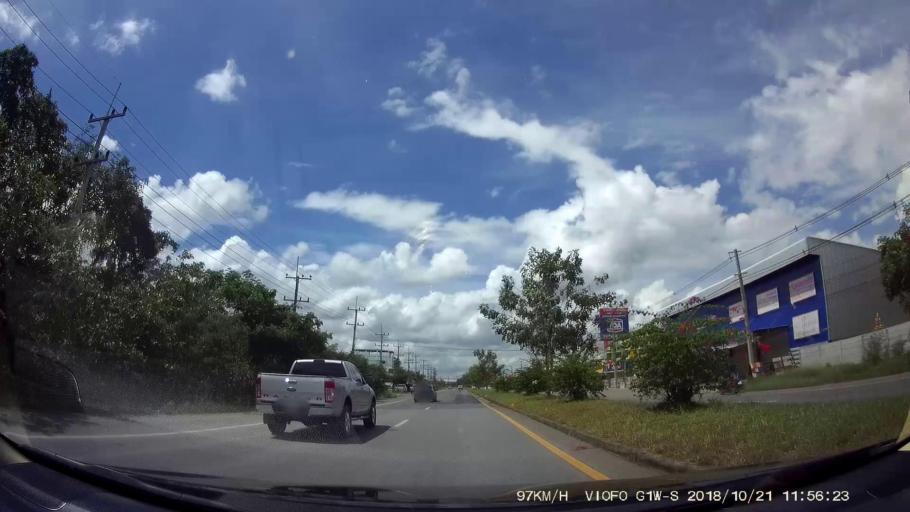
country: TH
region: Chaiyaphum
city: Chatturat
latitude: 15.5787
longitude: 101.8765
